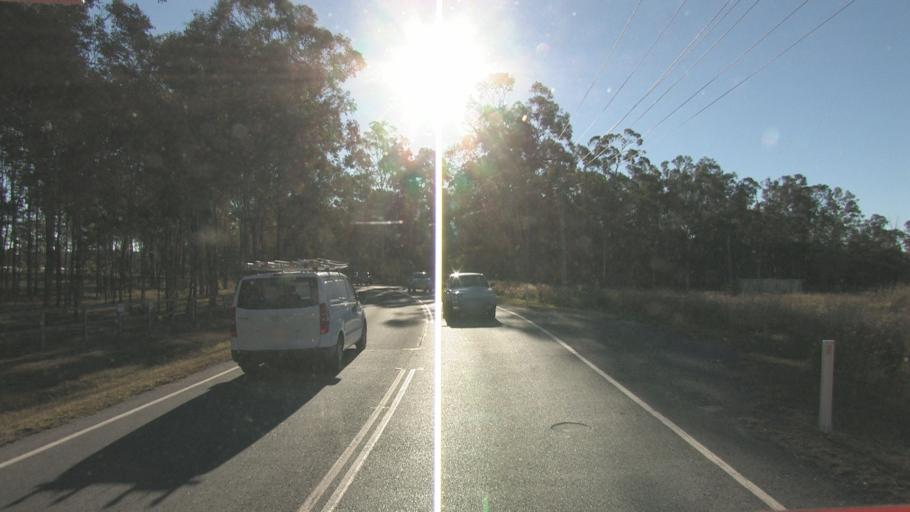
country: AU
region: Queensland
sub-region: Logan
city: Chambers Flat
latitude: -27.7471
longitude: 153.0741
